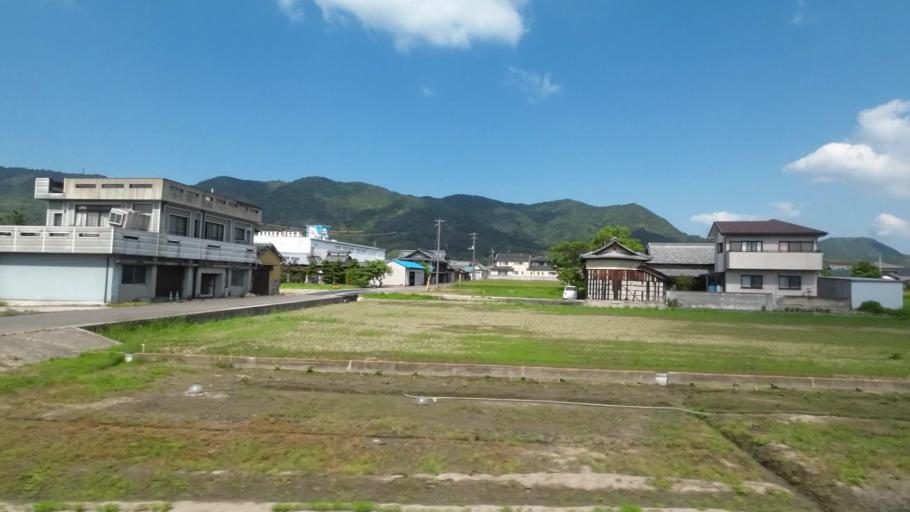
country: JP
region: Kagawa
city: Kan'onjicho
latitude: 34.1719
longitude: 133.6919
